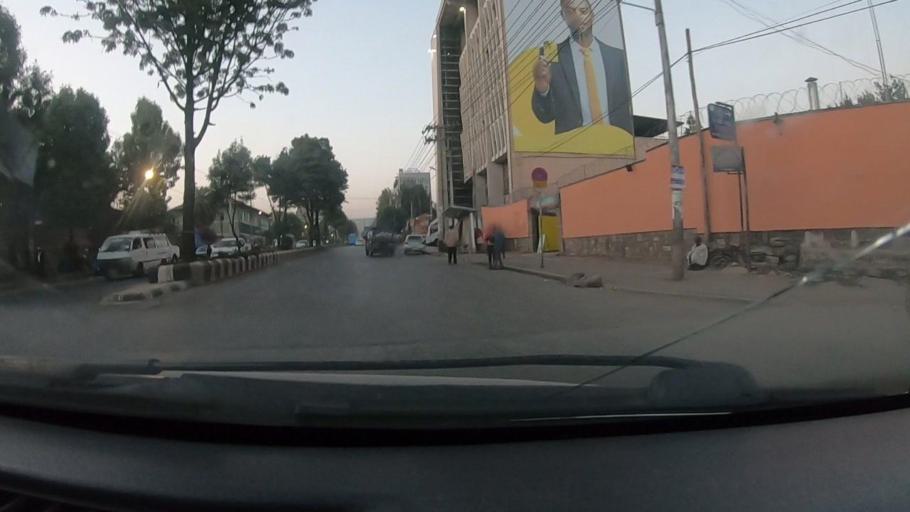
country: ET
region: Adis Abeba
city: Addis Ababa
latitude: 9.0425
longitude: 38.7498
